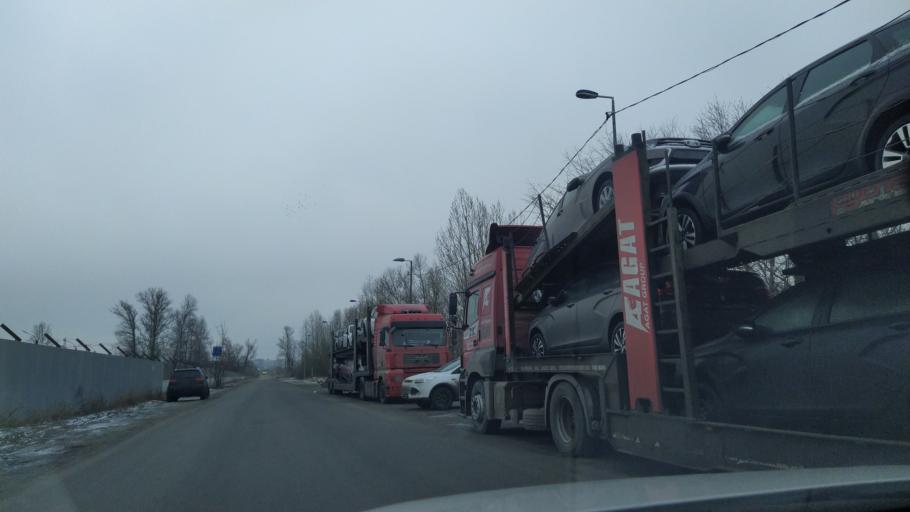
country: RU
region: St.-Petersburg
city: Dachnoye
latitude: 59.8072
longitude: 30.3094
